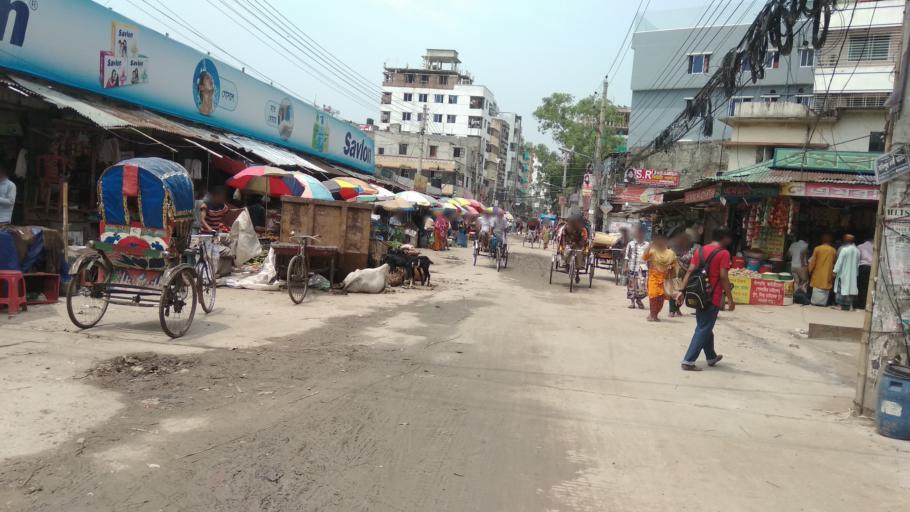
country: BD
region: Dhaka
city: Azimpur
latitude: 23.8041
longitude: 90.3642
